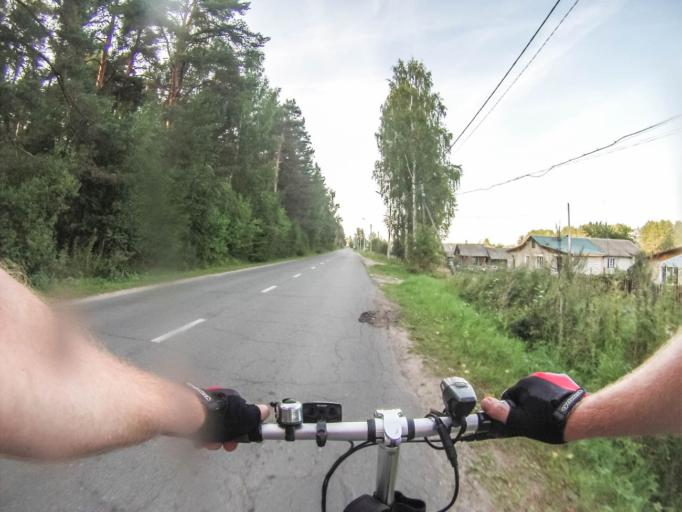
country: RU
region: Jaroslavl
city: Myshkin
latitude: 57.7720
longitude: 38.4428
